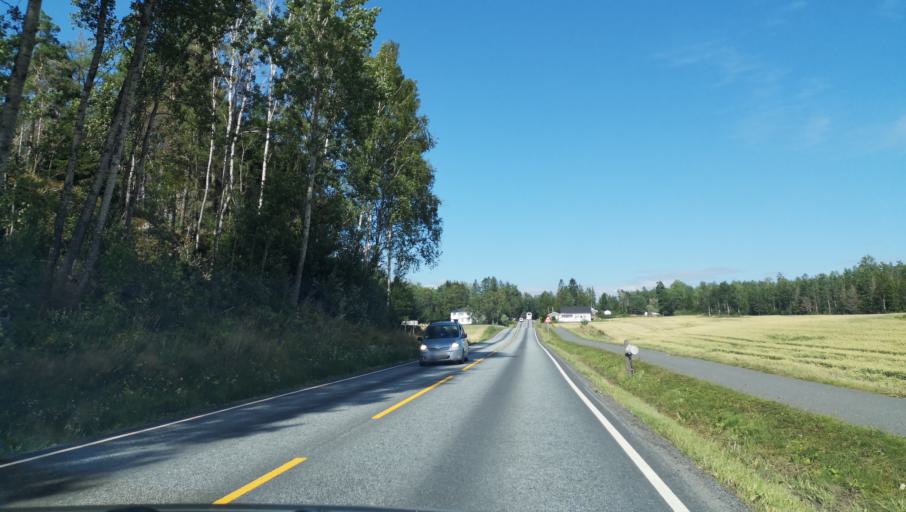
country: NO
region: Ostfold
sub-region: Valer
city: Kirkebygda
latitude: 59.5631
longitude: 10.8526
